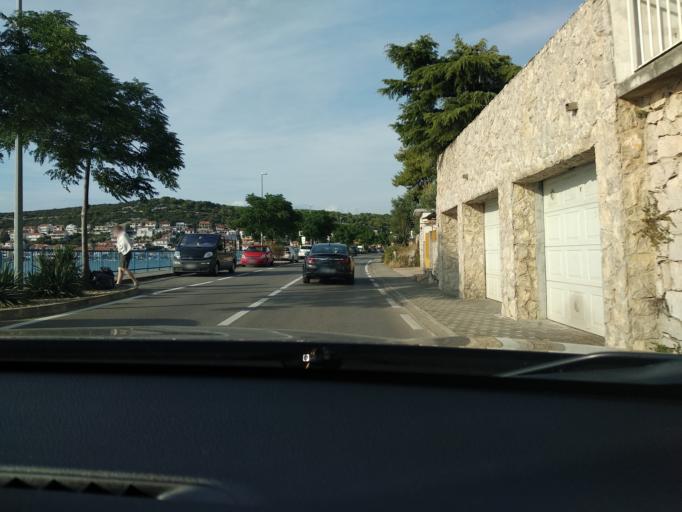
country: HR
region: Sibensko-Kniniska
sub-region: Grad Sibenik
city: Tisno
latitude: 43.7975
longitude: 15.6347
